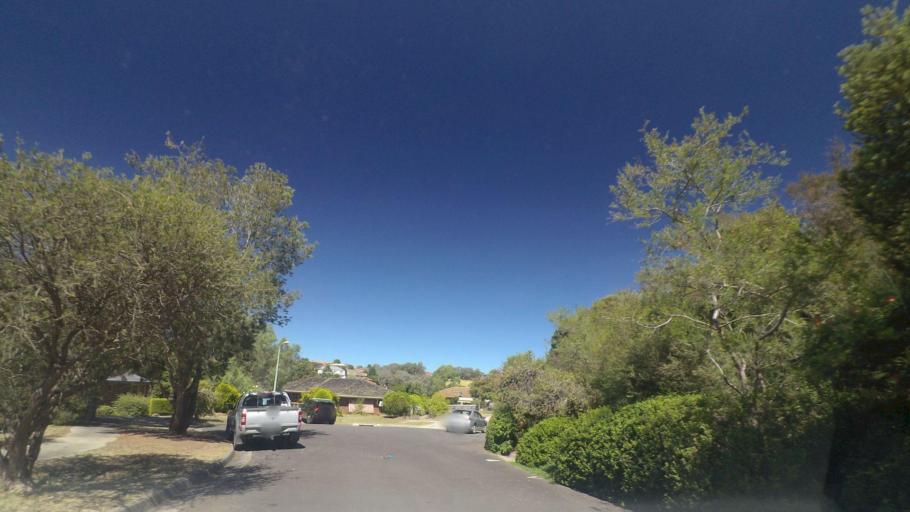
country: AU
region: Victoria
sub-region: Manningham
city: Donvale
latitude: -37.7687
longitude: 145.1738
